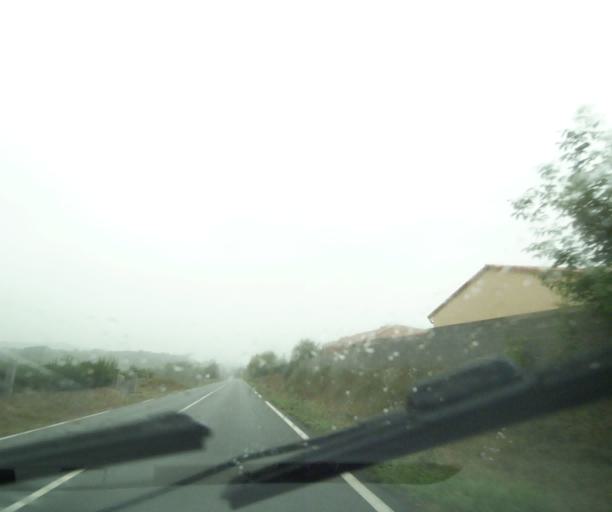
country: FR
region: Auvergne
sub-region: Departement du Puy-de-Dome
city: Nohanent
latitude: 45.8180
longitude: 3.0590
